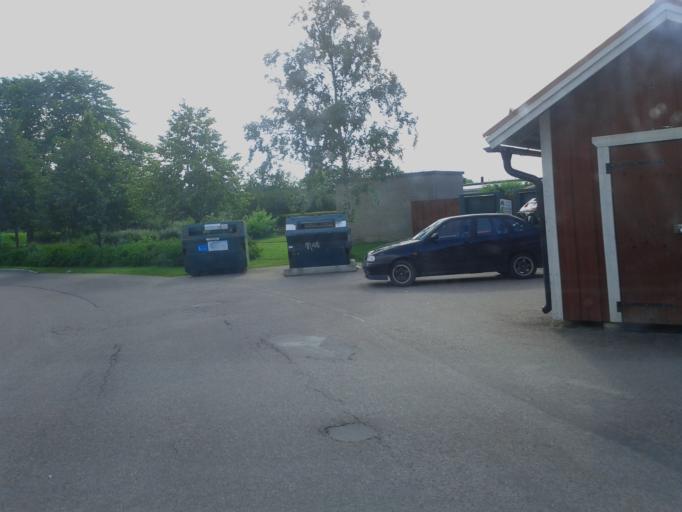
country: SE
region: Vaestmanland
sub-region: Sala Kommun
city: Sala
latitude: 59.9233
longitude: 16.5863
